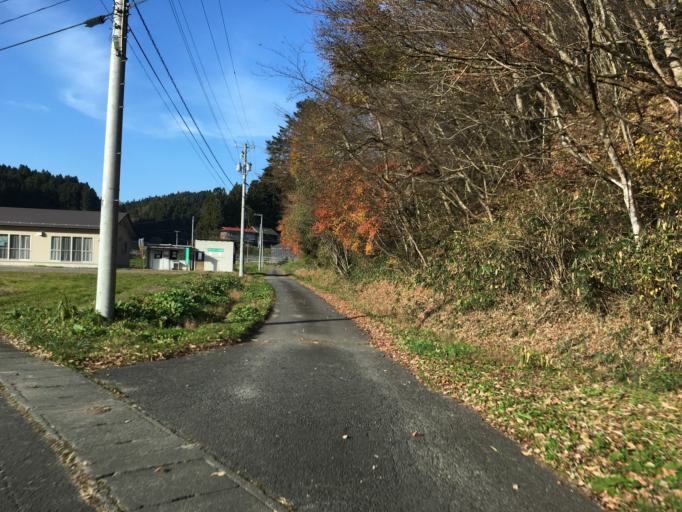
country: JP
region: Fukushima
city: Ishikawa
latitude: 37.2393
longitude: 140.5884
